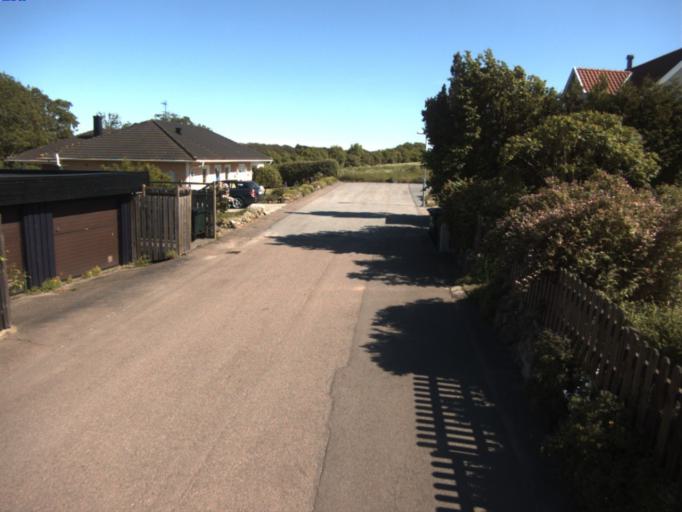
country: SE
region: Skane
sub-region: Helsingborg
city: Gantofta
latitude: 55.9864
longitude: 12.8110
